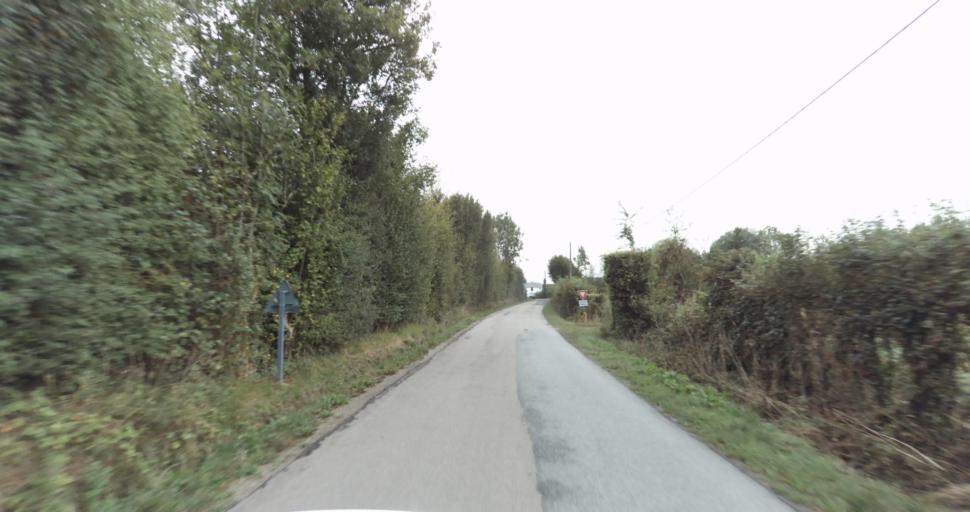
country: FR
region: Lower Normandy
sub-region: Departement de l'Orne
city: Trun
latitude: 48.8961
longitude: 0.1099
